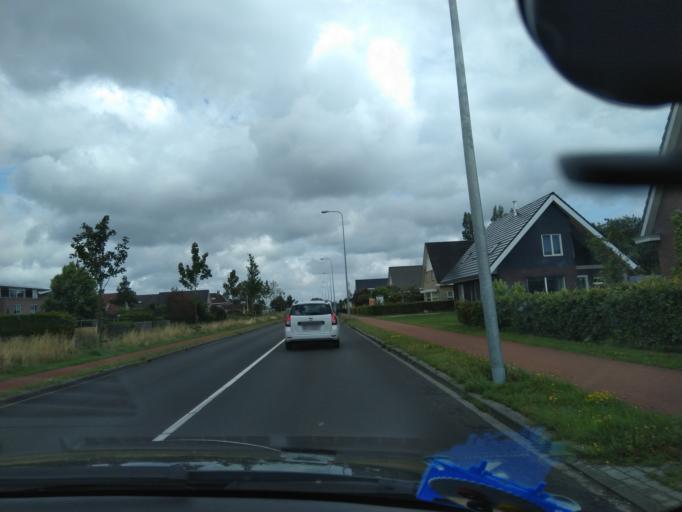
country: NL
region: Groningen
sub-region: Gemeente Groningen
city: Groningen
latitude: 53.2017
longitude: 6.5139
